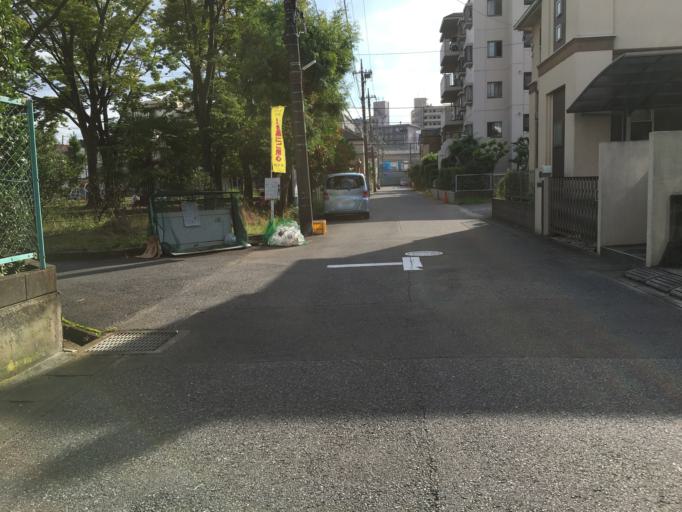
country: JP
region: Chiba
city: Matsudo
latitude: 35.7940
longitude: 139.9065
